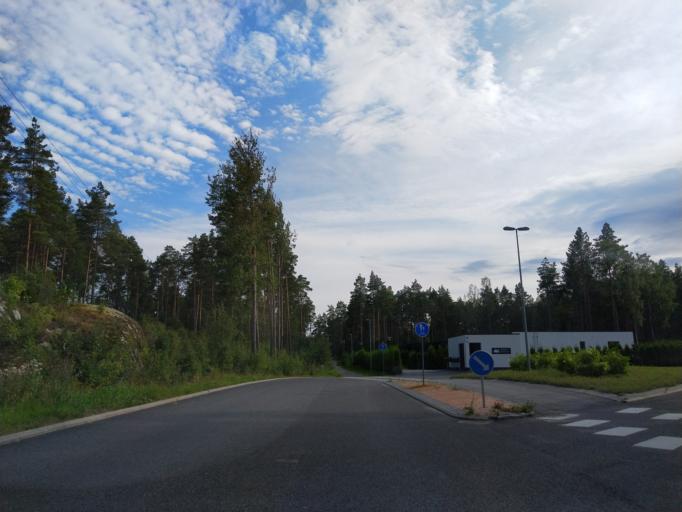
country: FI
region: Varsinais-Suomi
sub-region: Turku
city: Turku
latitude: 60.4229
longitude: 22.2134
